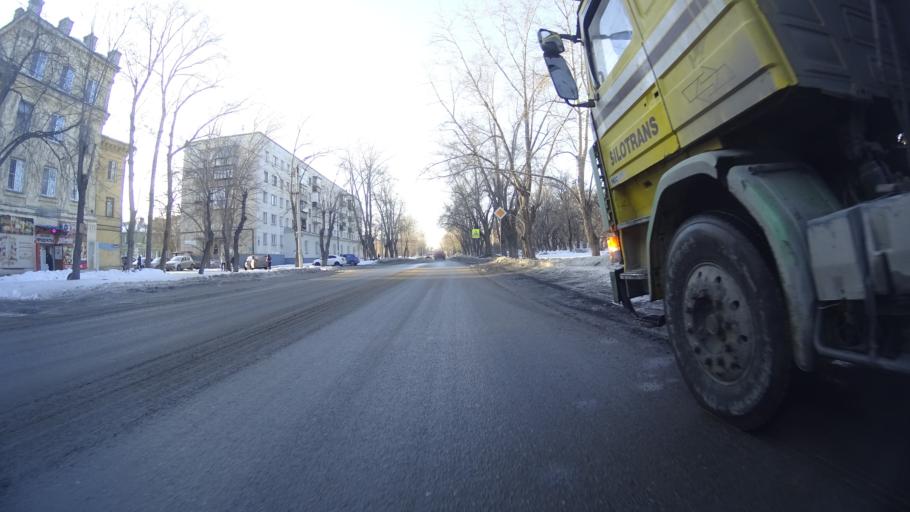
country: RU
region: Chelyabinsk
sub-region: Gorod Chelyabinsk
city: Chelyabinsk
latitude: 55.1285
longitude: 61.4681
